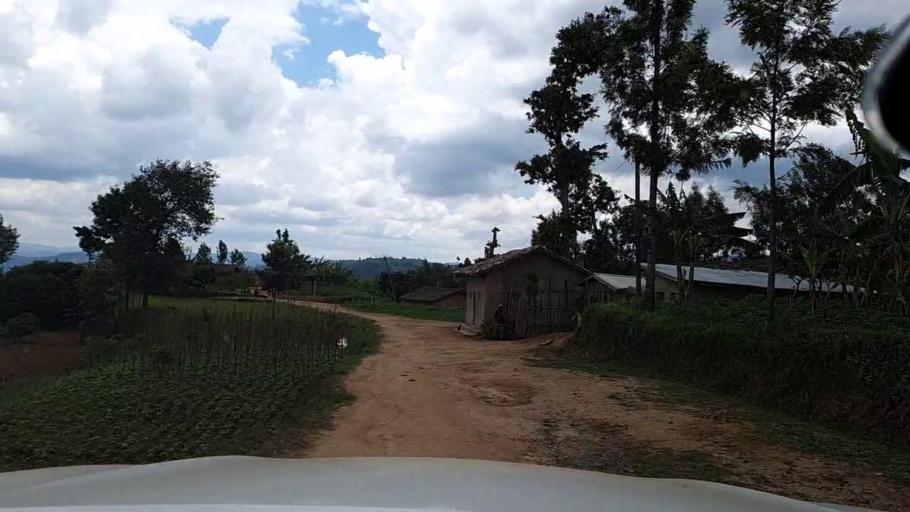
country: RW
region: Southern Province
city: Nzega
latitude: -2.6367
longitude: 29.4848
